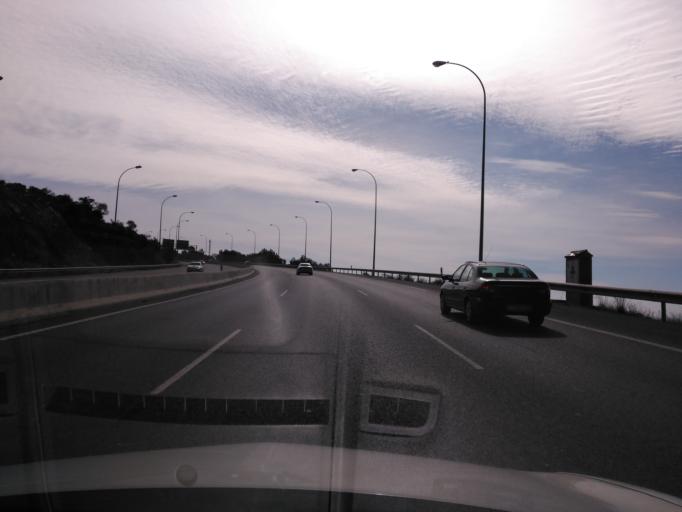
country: ES
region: Andalusia
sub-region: Provincia de Malaga
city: Malaga
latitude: 36.7527
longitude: -4.4154
